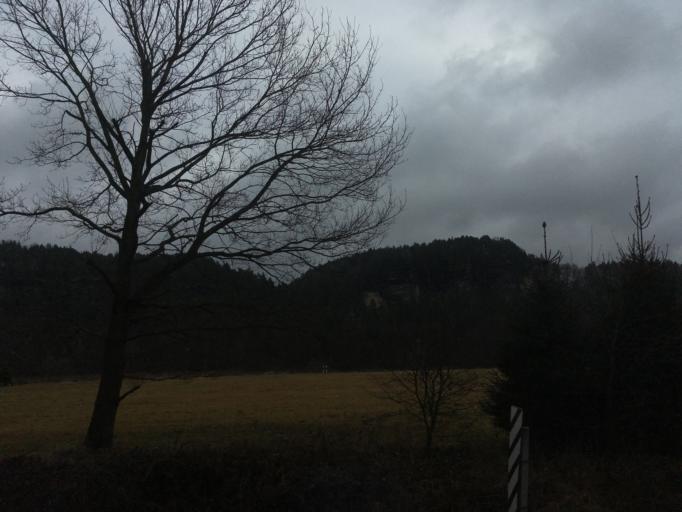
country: DE
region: Saxony
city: Konigstein
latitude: 50.9502
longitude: 14.0823
